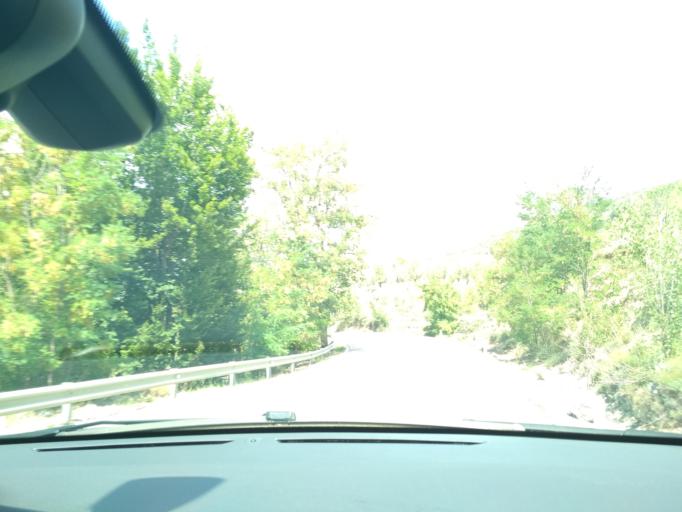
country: ES
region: Aragon
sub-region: Provincia de Teruel
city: Rubielos de Mora
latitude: 40.1904
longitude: -0.6465
